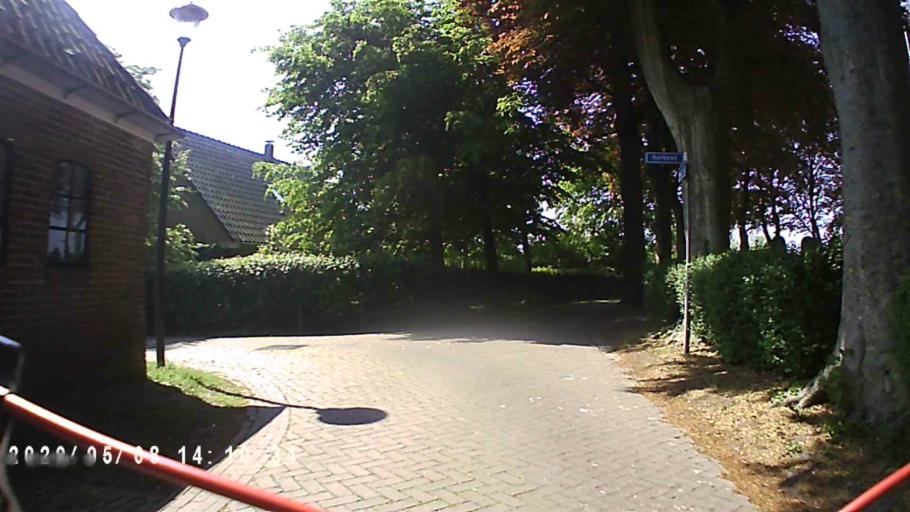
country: NL
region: Groningen
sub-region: Gemeente Appingedam
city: Appingedam
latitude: 53.3460
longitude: 6.7975
